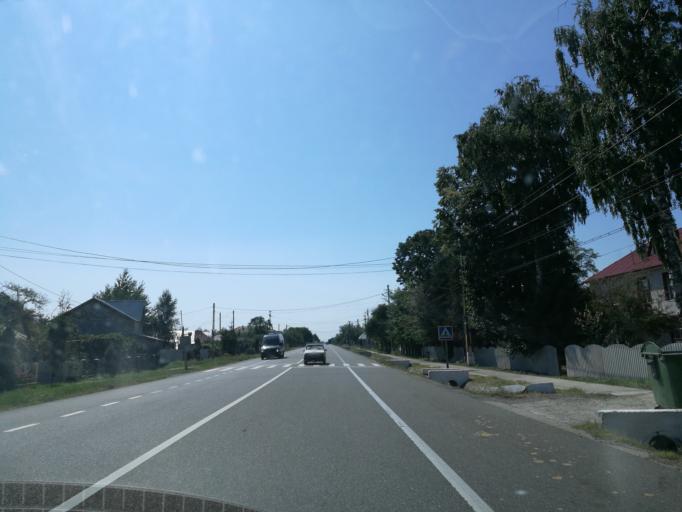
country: RO
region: Bacau
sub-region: Comuna Filipesti
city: Filipesti
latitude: 46.7417
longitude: 26.8853
